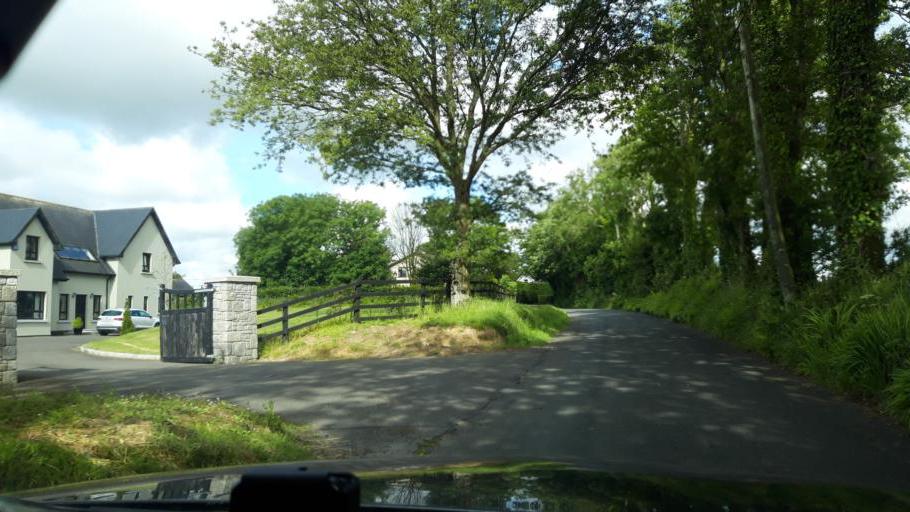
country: IE
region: Leinster
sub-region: Loch Garman
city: Loch Garman
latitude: 52.2855
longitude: -6.5106
